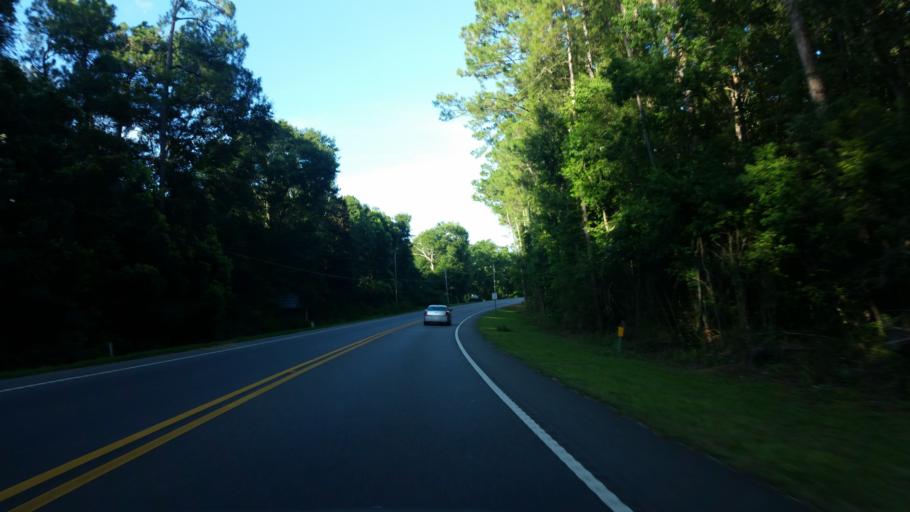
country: US
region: Alabama
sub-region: Baldwin County
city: Elberta
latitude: 30.4136
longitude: -87.6104
